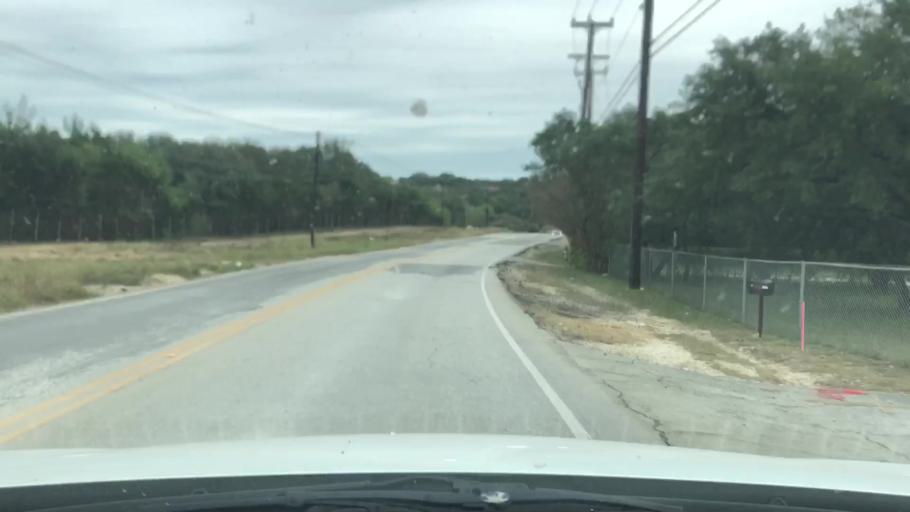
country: US
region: Texas
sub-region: Bexar County
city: Timberwood Park
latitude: 29.6486
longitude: -98.4167
